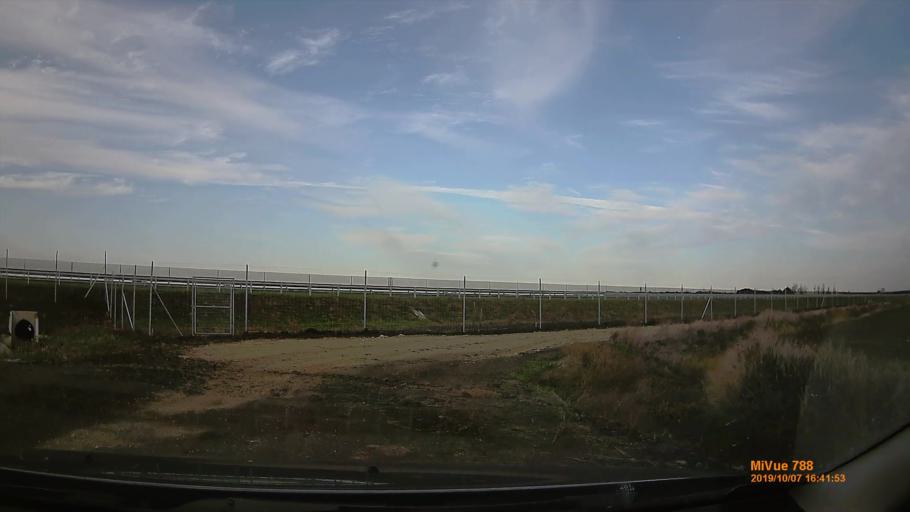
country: HU
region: Bekes
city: Szarvas
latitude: 46.8193
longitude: 20.5943
